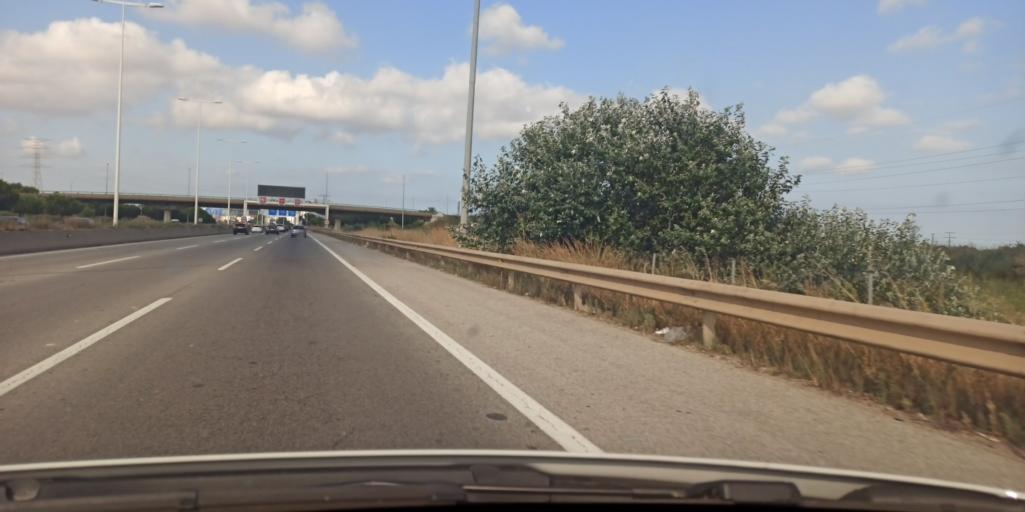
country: ES
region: Catalonia
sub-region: Provincia de Barcelona
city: Cornella de Llobregat
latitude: 41.3354
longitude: 2.0801
